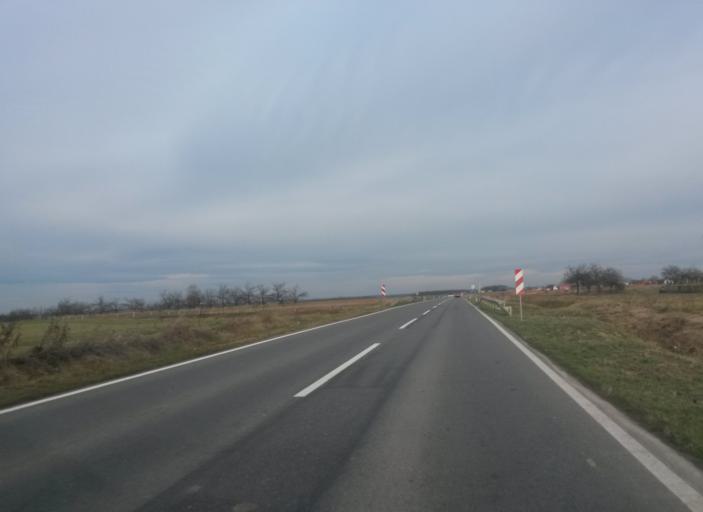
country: HR
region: Osjecko-Baranjska
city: Cepin
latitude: 45.5259
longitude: 18.5416
